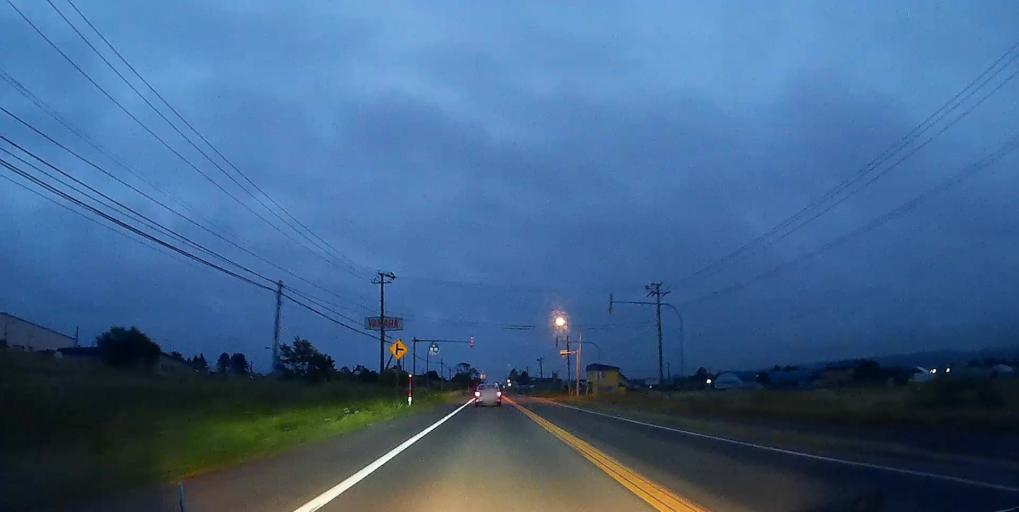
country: JP
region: Hokkaido
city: Nanae
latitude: 42.2206
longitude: 140.3745
